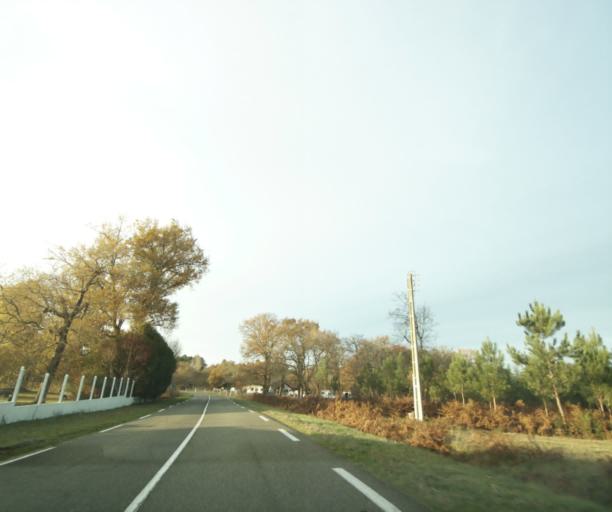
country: FR
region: Aquitaine
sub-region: Departement des Landes
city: Gabarret
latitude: 44.0973
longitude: -0.1002
